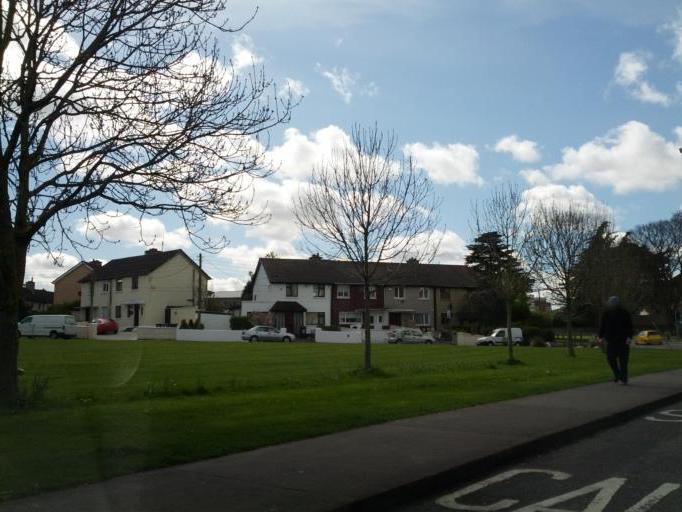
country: IE
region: Leinster
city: Clondalkin
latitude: 53.3243
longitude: -6.3915
